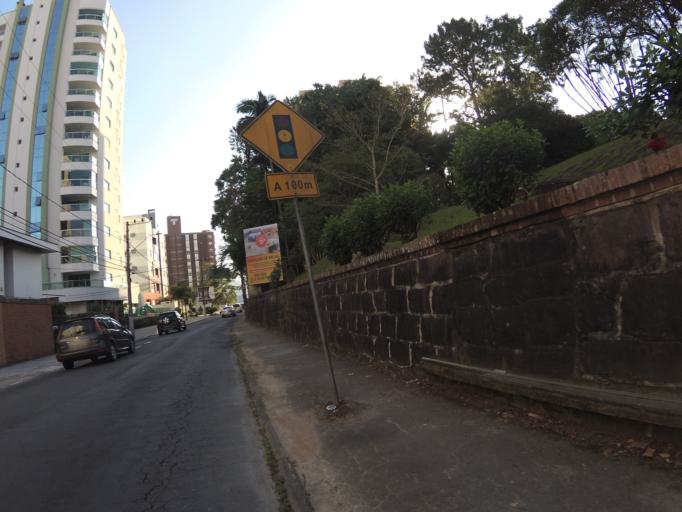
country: BR
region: Santa Catarina
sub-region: Blumenau
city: Blumenau
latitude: -26.9081
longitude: -49.0759
